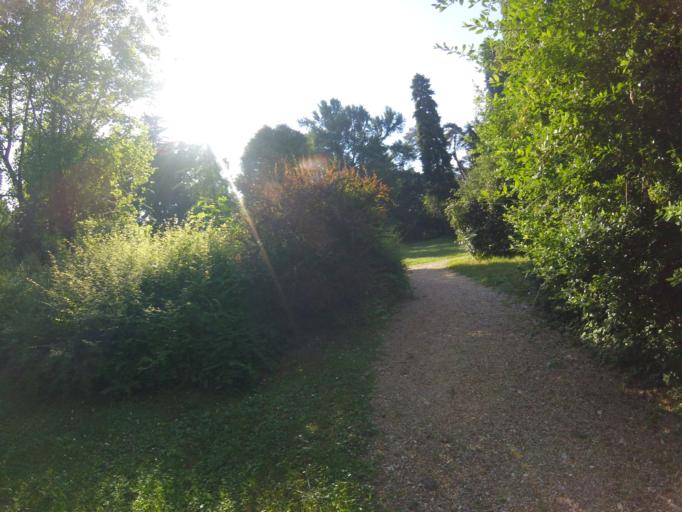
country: HU
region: Baranya
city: Sellye
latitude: 45.8705
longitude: 17.8485
